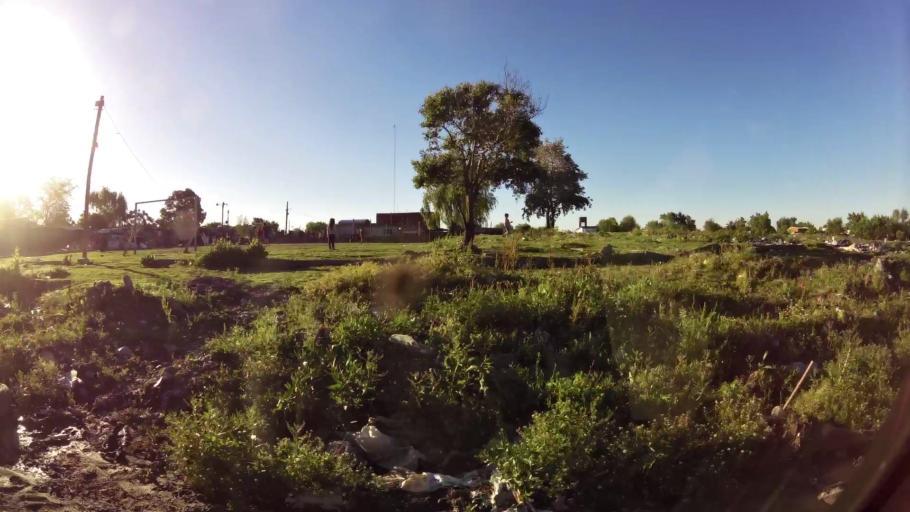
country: AR
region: Buenos Aires
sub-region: Partido de Almirante Brown
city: Adrogue
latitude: -34.7762
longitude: -58.3403
